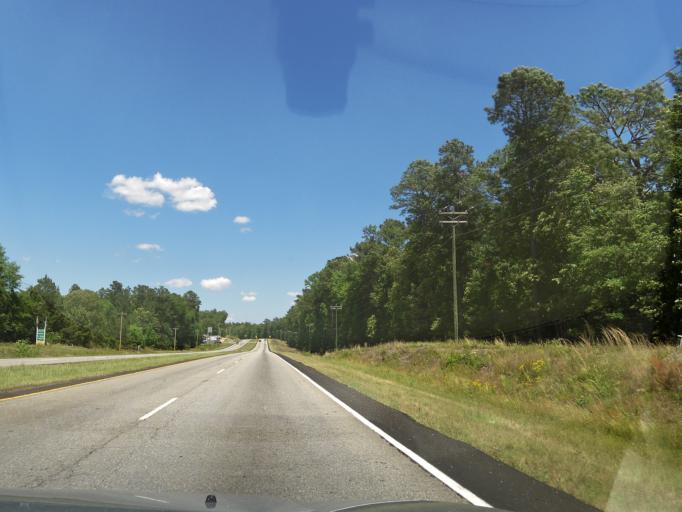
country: US
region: South Carolina
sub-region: Aiken County
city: Gloverville
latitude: 33.5423
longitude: -81.8272
